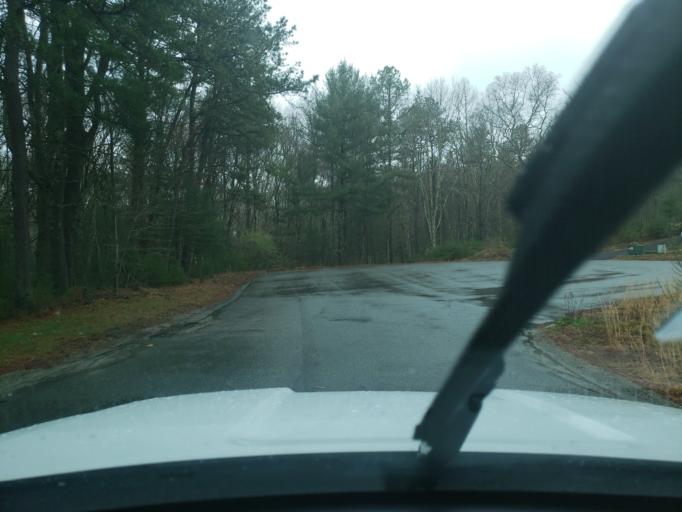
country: US
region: Connecticut
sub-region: Windham County
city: Moosup
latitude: 41.6915
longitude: -71.8260
